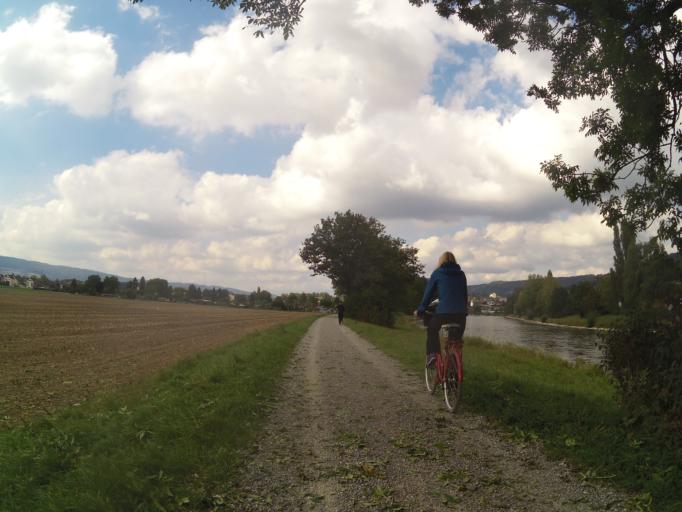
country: CH
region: Zurich
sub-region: Bezirk Dietikon
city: Oberengstringen / Rauchacher
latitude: 47.4049
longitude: 8.4570
